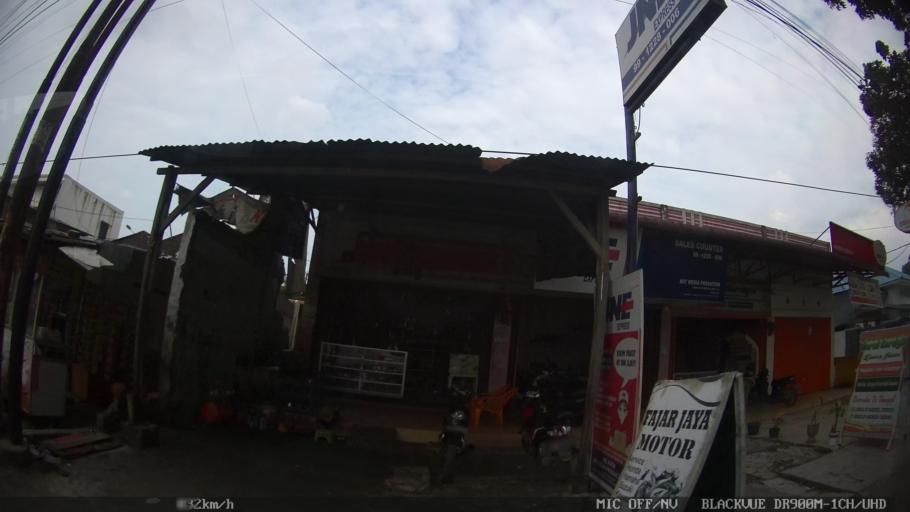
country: ID
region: North Sumatra
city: Deli Tua
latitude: 3.5435
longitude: 98.6796
